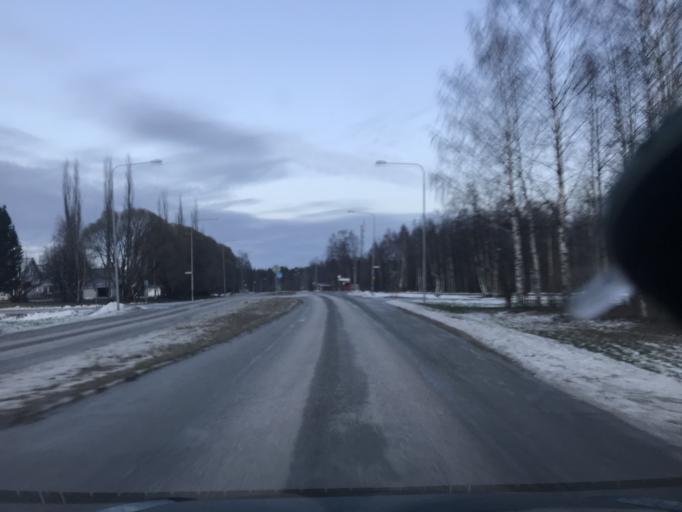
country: SE
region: Norrbotten
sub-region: Lulea Kommun
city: Sodra Sunderbyn
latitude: 65.6528
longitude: 21.9646
